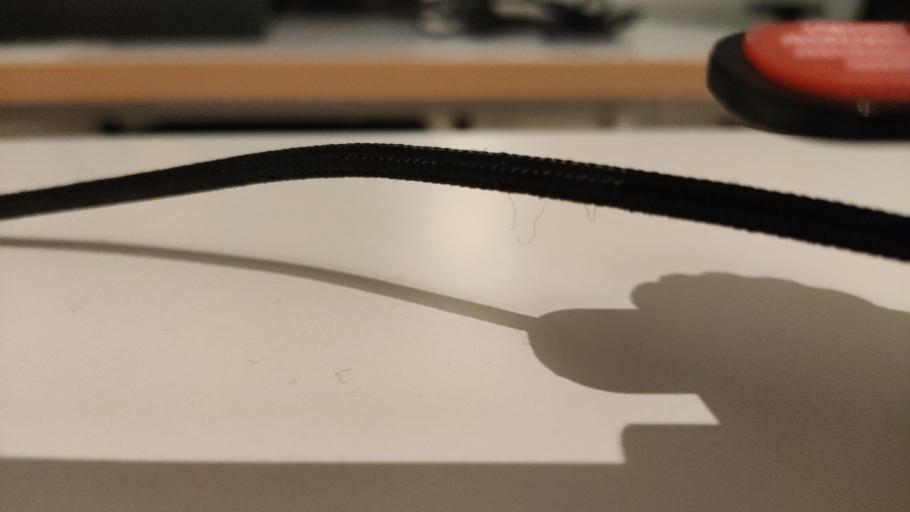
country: RU
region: Moskovskaya
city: Rogachevo
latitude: 56.4396
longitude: 37.1783
